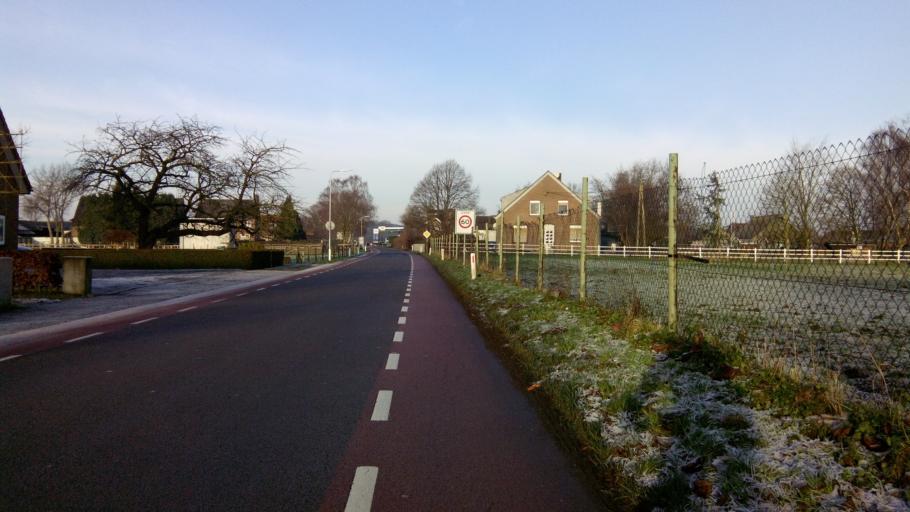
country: NL
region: Gelderland
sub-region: Gemeente Groesbeek
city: De Horst
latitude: 51.8058
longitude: 5.9653
